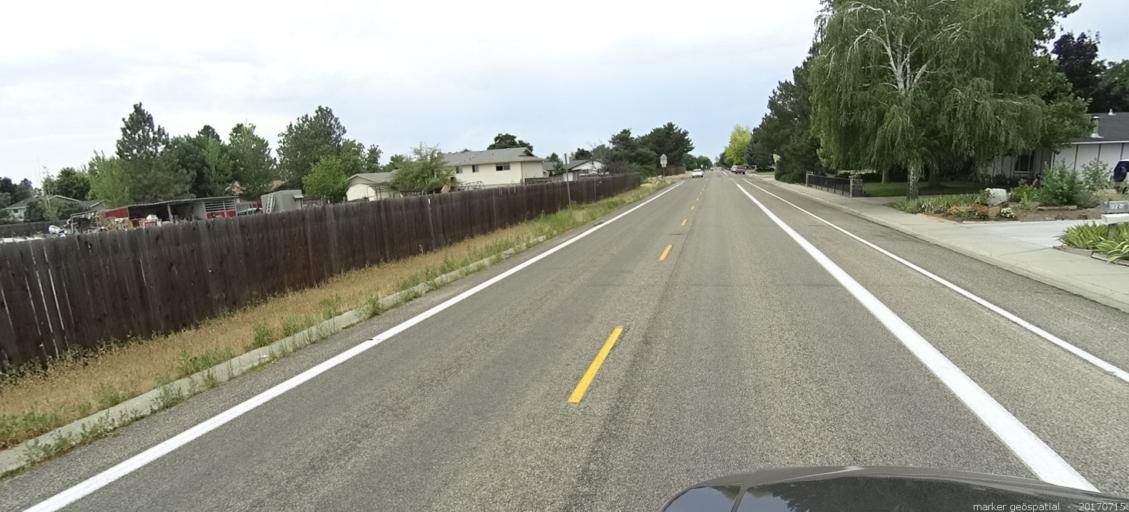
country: US
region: Idaho
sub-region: Ada County
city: Garden City
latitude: 43.5540
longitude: -116.2780
